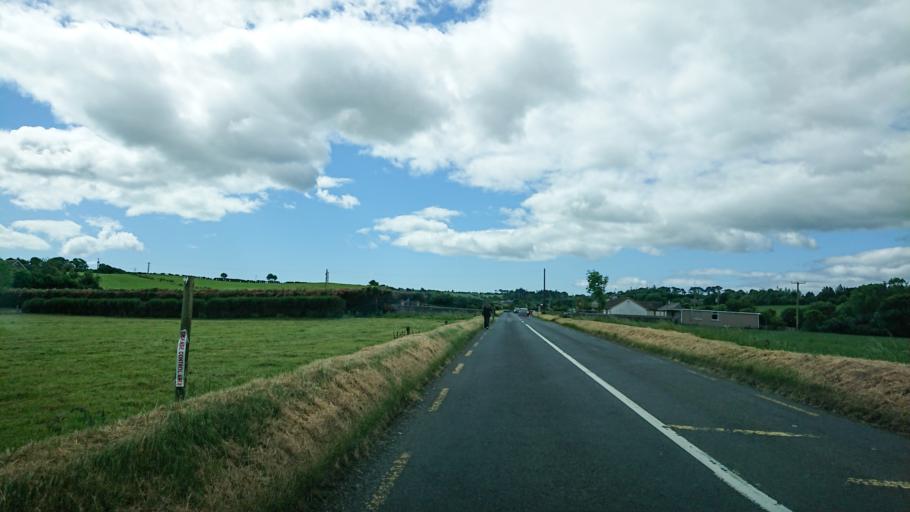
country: IE
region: Leinster
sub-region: Kilkenny
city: Mooncoin
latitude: 52.2284
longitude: -7.1999
